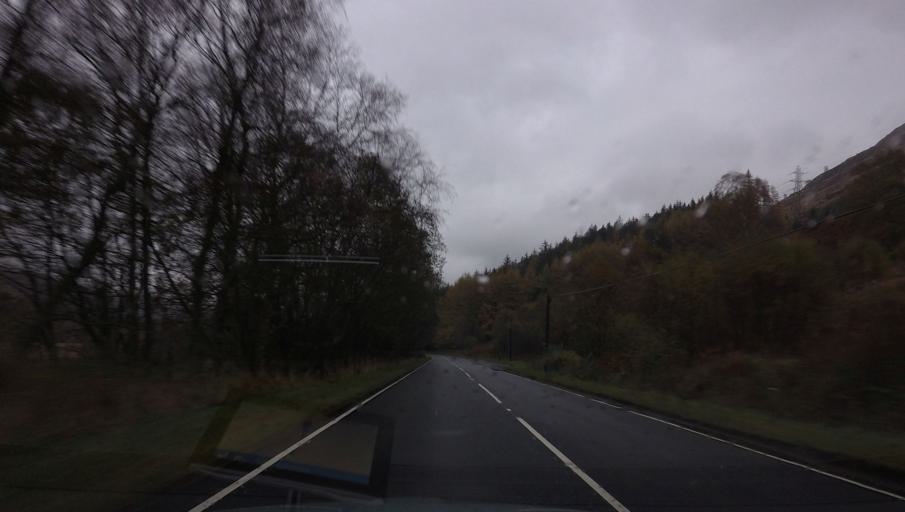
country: GB
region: Scotland
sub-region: Argyll and Bute
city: Garelochhead
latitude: 56.3911
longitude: -4.5954
